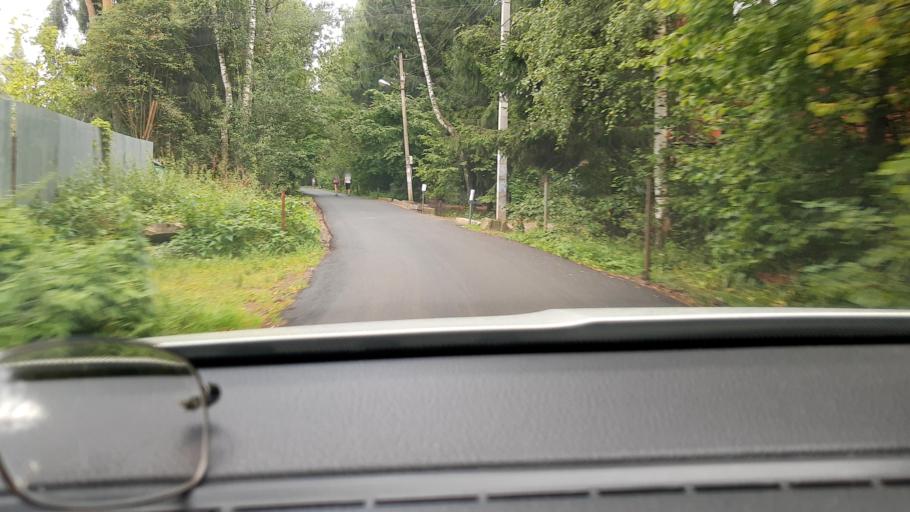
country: RU
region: Moskovskaya
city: Kokoshkino
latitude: 55.5932
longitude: 37.1630
